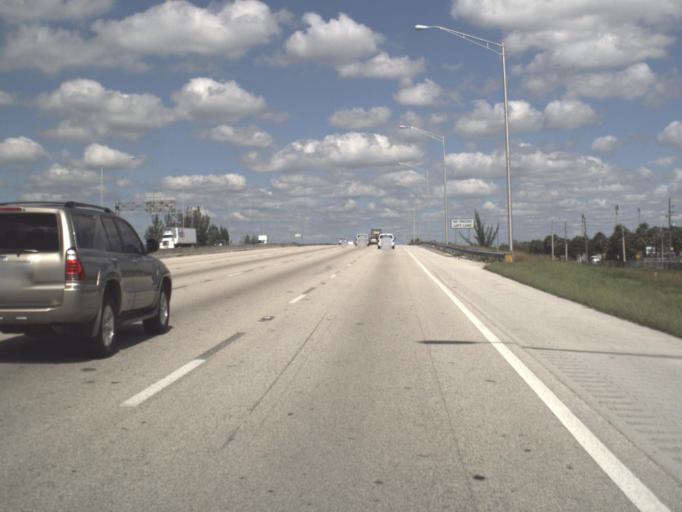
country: US
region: Florida
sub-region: Miami-Dade County
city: Doral
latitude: 25.8233
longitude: -80.3865
